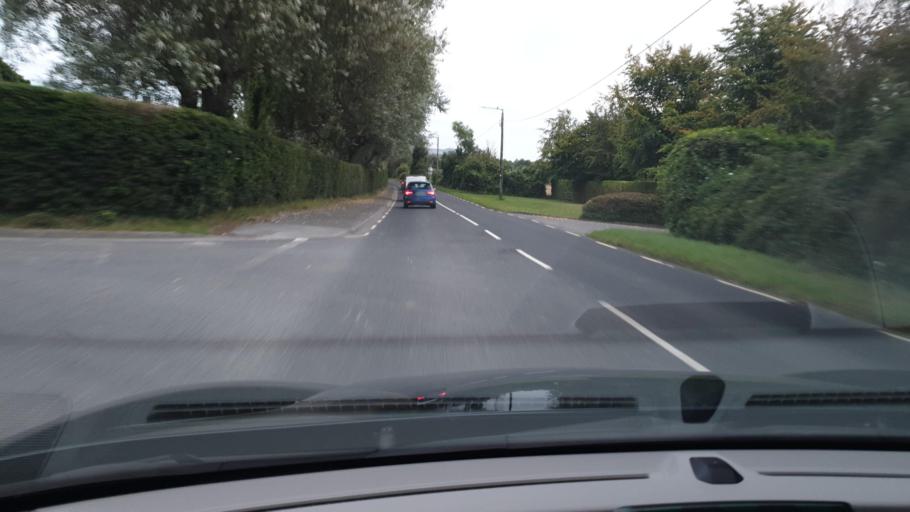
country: IE
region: Leinster
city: Kinsealy-Drinan
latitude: 53.4348
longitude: -6.1831
